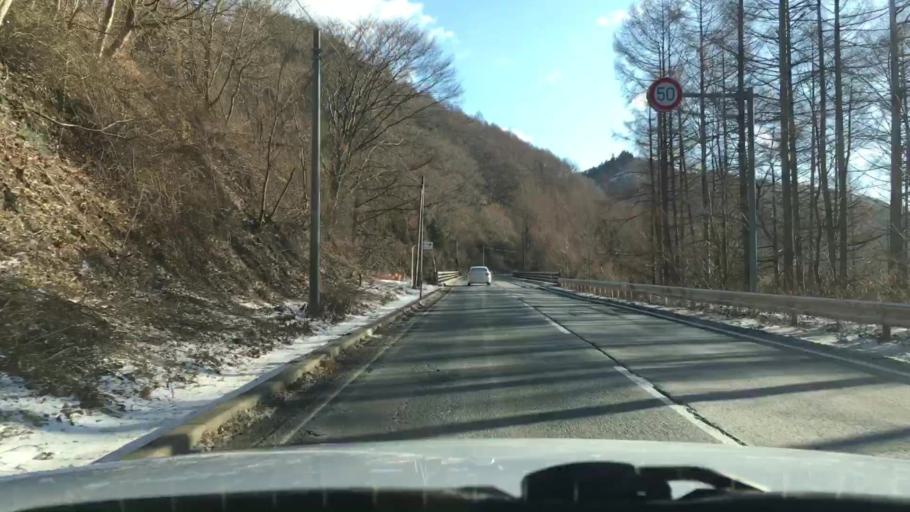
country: JP
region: Iwate
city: Morioka-shi
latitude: 39.6662
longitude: 141.3100
